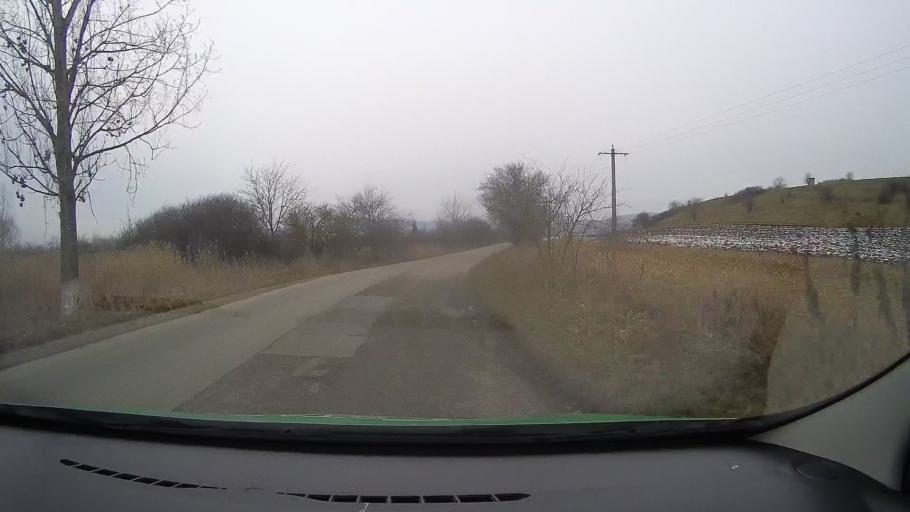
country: RO
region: Hunedoara
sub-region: Comuna Romos
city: Romos
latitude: 45.8784
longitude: 23.2600
